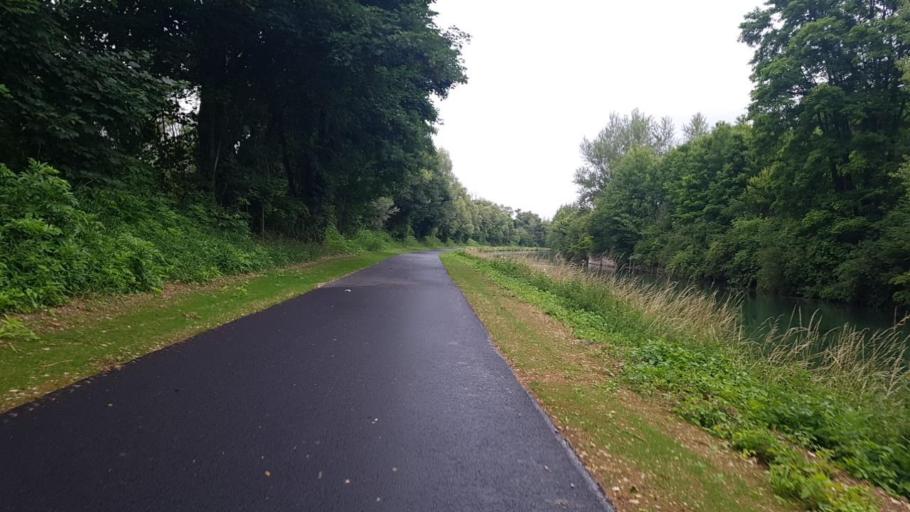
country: FR
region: Champagne-Ardenne
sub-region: Departement de la Marne
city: Vitry-le-Francois
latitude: 48.7754
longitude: 4.5443
